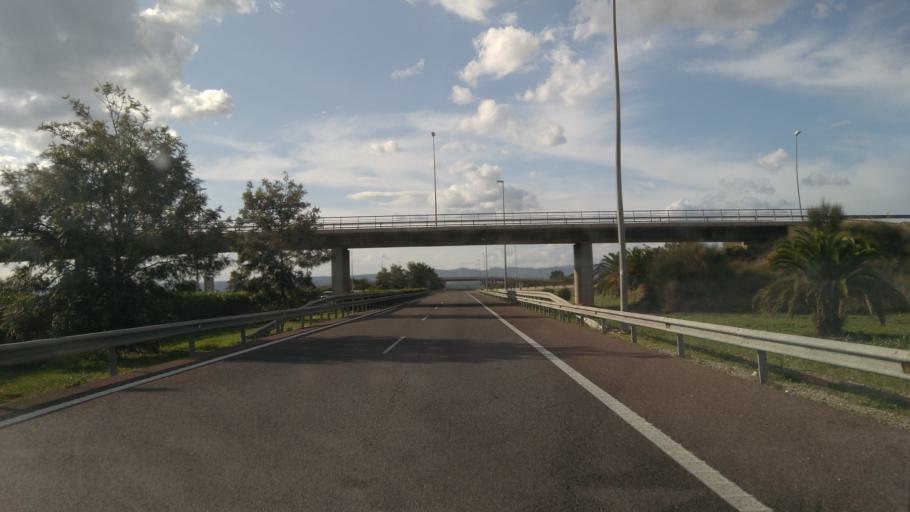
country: ES
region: Valencia
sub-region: Provincia de Valencia
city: Guadassuar
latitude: 39.1776
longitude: -0.4751
